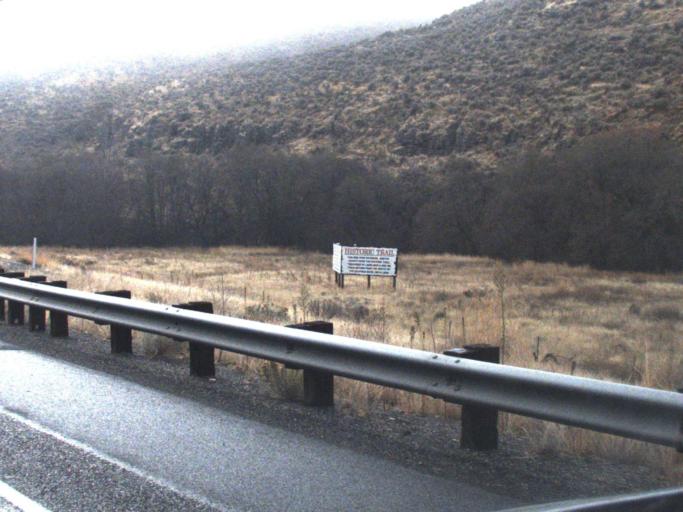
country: US
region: Washington
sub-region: Asotin County
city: Clarkston Heights-Vineland
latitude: 46.4109
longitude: -117.2681
